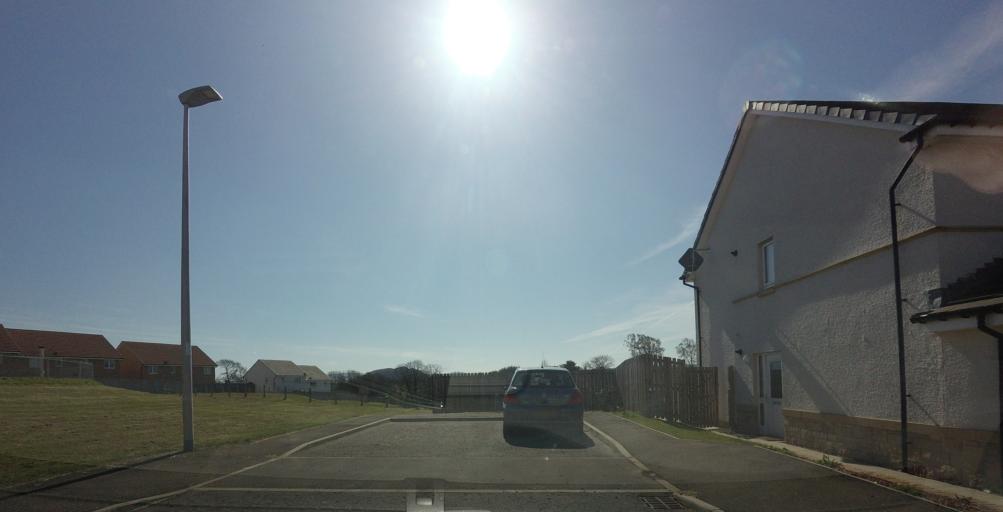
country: GB
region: Scotland
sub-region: West Lothian
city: Blackburn
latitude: 55.8700
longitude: -3.6118
